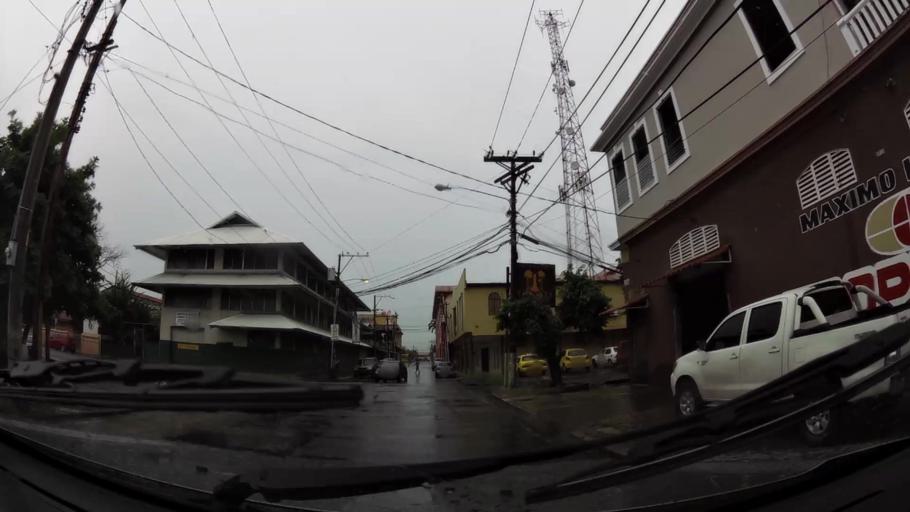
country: PA
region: Colon
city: Colon
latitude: 9.3642
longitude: -79.9045
